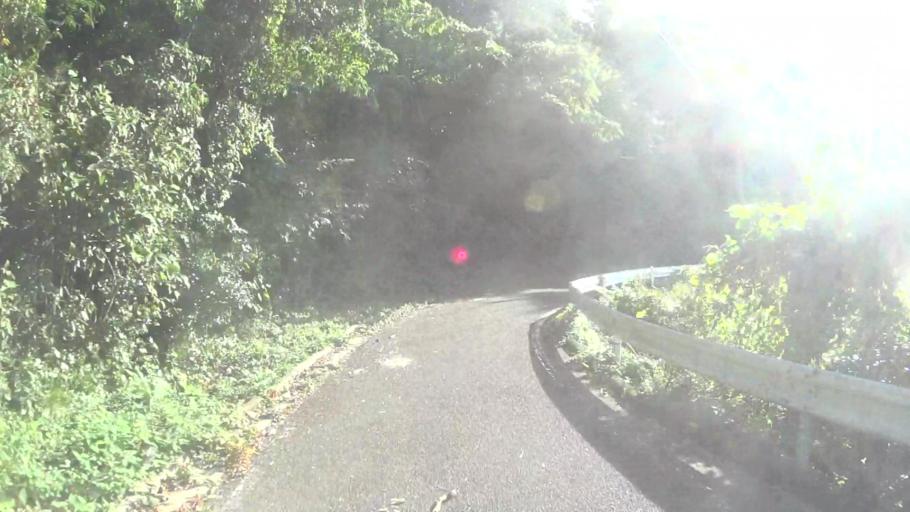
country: JP
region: Kyoto
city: Maizuru
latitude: 35.5661
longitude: 135.4106
